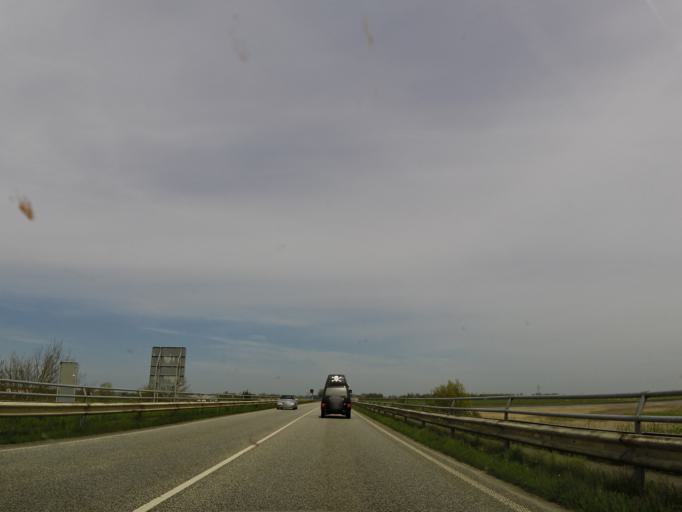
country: DE
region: Schleswig-Holstein
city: Tonning
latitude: 54.3113
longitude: 8.9576
